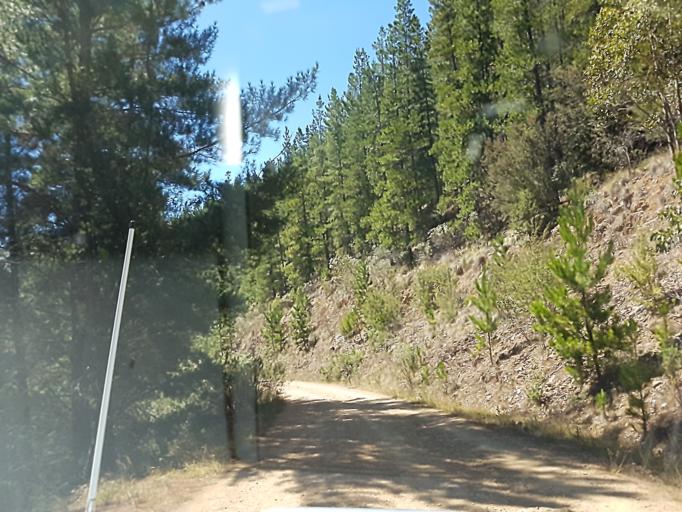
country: AU
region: Victoria
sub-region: Alpine
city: Mount Beauty
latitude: -36.7463
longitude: 146.9589
